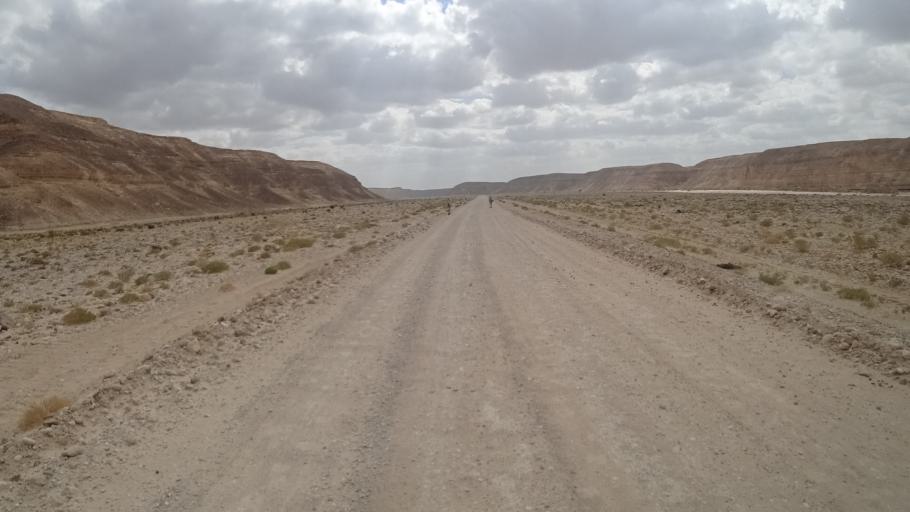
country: YE
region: Al Mahrah
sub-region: Shahan
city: Shihan as Sufla
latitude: 17.4596
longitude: 53.0082
